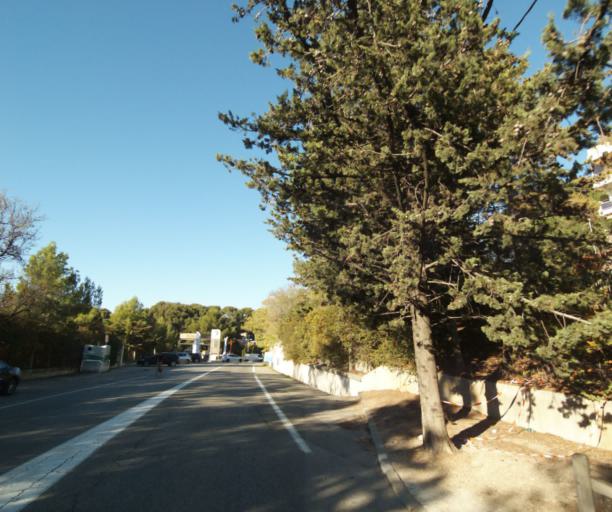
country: FR
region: Provence-Alpes-Cote d'Azur
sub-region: Departement des Bouches-du-Rhone
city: Cassis
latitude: 43.2207
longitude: 5.5439
